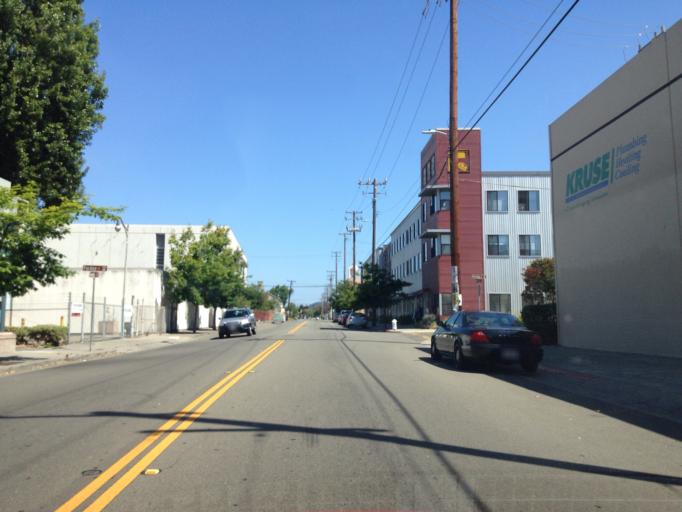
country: US
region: California
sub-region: Alameda County
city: Berkeley
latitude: 37.8558
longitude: -122.2926
